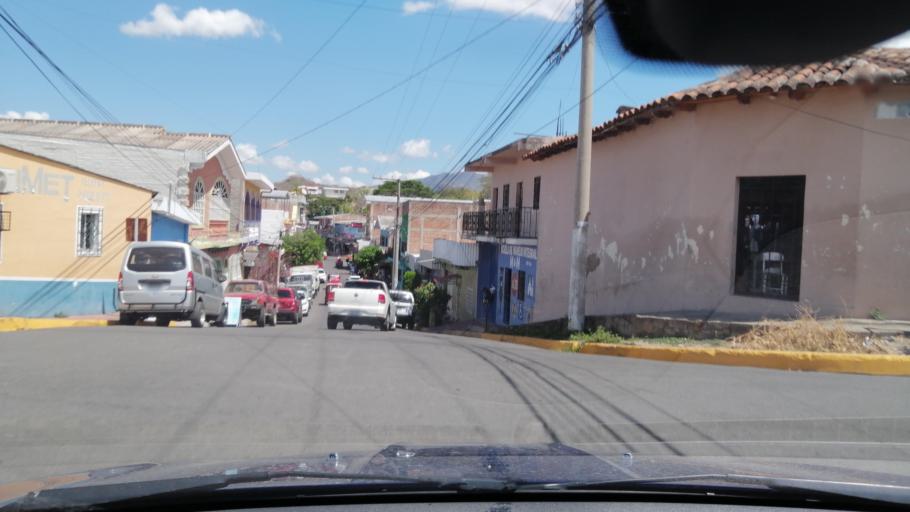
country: SV
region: Santa Ana
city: Metapan
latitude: 14.3293
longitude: -89.4438
